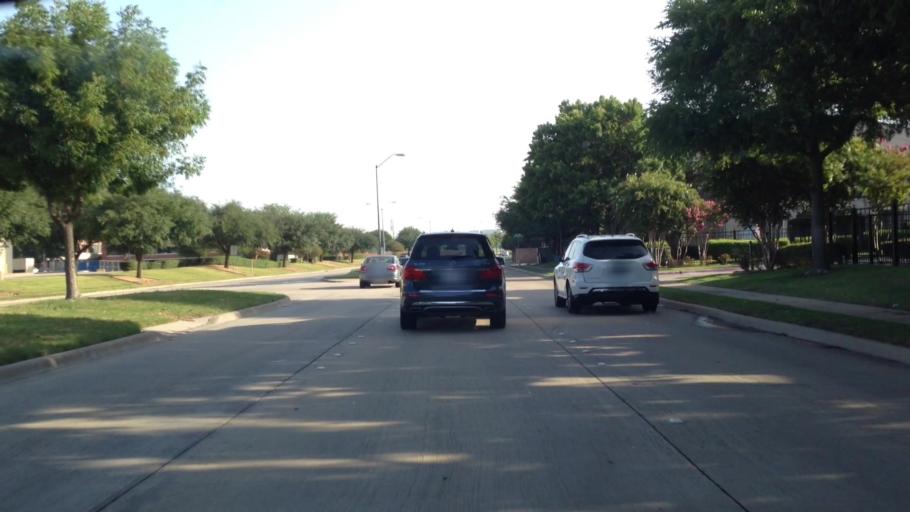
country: US
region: Texas
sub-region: Denton County
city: The Colony
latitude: 33.0487
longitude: -96.8265
